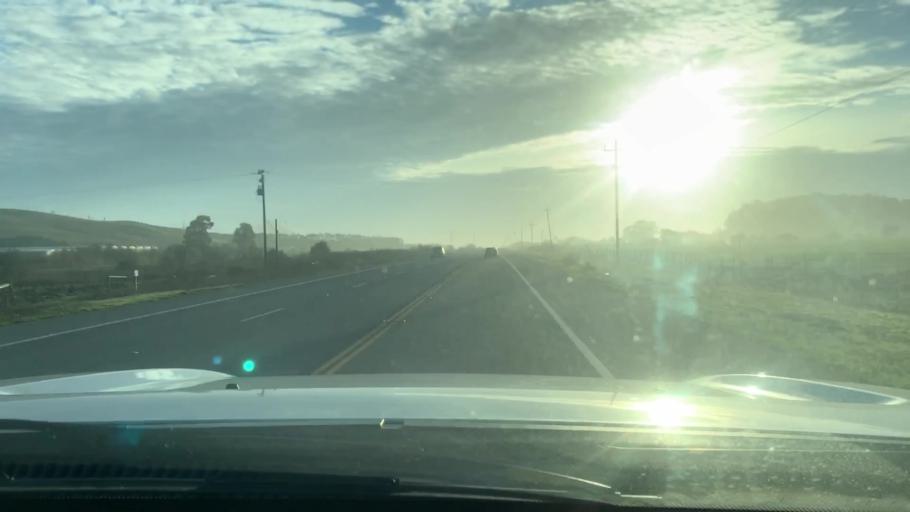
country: US
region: California
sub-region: San Luis Obispo County
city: Los Osos
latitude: 35.2908
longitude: -120.7502
